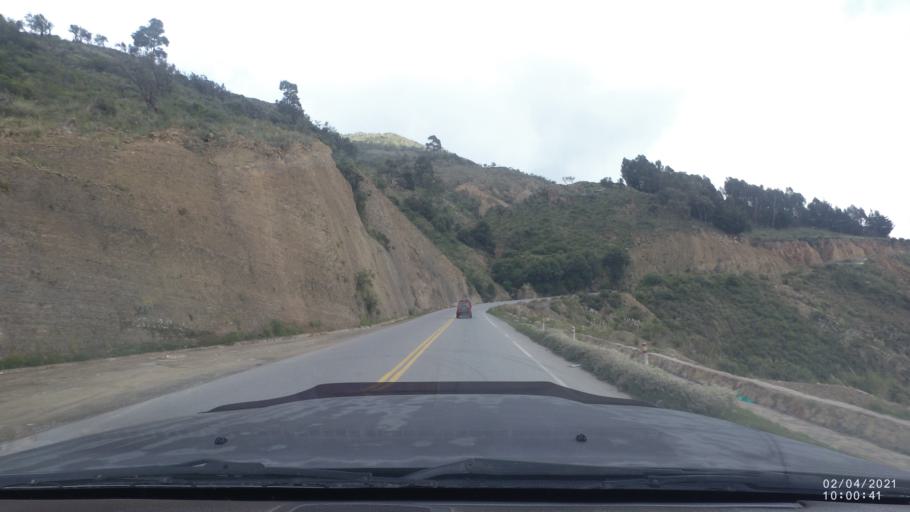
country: BO
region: Cochabamba
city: Irpa Irpa
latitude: -17.6751
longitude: -66.4299
